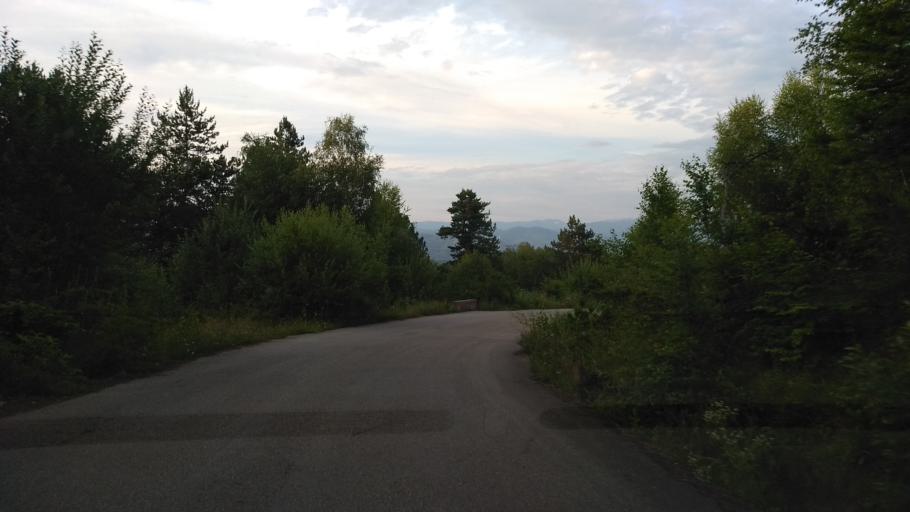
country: RO
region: Hunedoara
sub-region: Municipiul  Vulcan
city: Jiu-Paroseni
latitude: 45.3529
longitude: 23.2883
